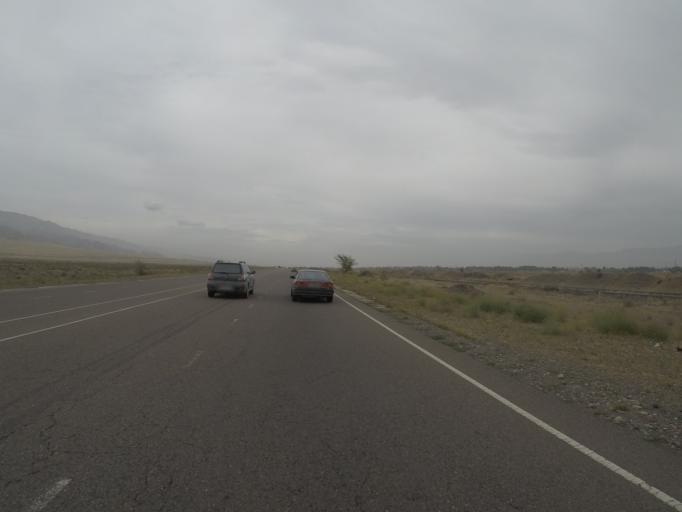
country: KG
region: Chuy
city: Bystrovka
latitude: 42.8300
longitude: 75.5011
